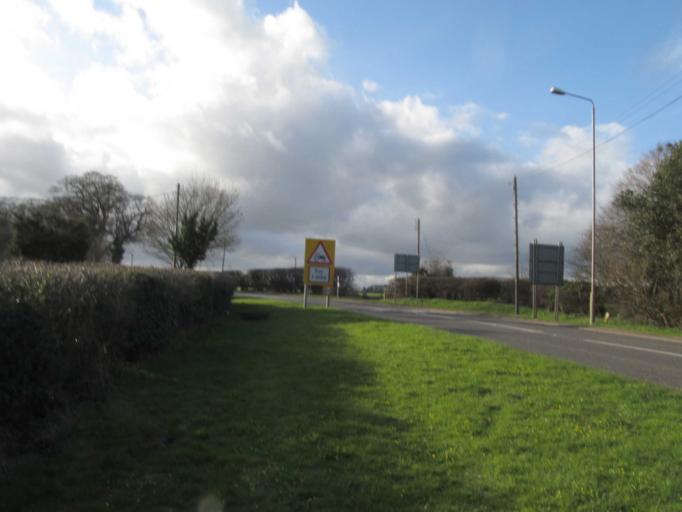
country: GB
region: England
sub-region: Nottinghamshire
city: East Leake
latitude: 52.8147
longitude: -1.1482
